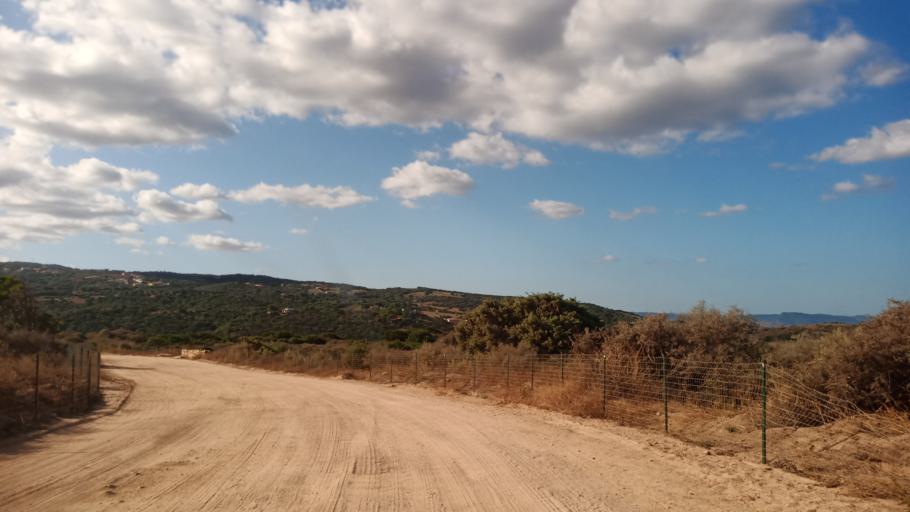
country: IT
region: Sardinia
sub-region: Provincia di Olbia-Tempio
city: Trinita d'Agultu
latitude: 41.0202
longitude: 8.8898
